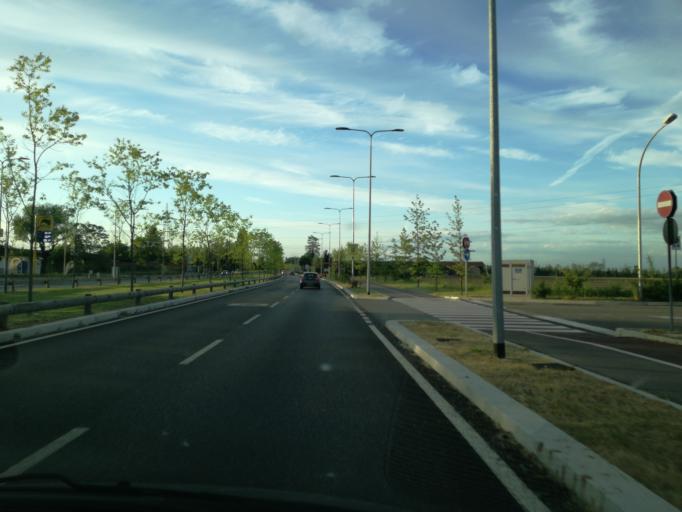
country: IT
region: Lombardy
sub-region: Citta metropolitana di Milano
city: Noverasco-Sporting Mirasole
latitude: 45.3981
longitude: 9.2105
